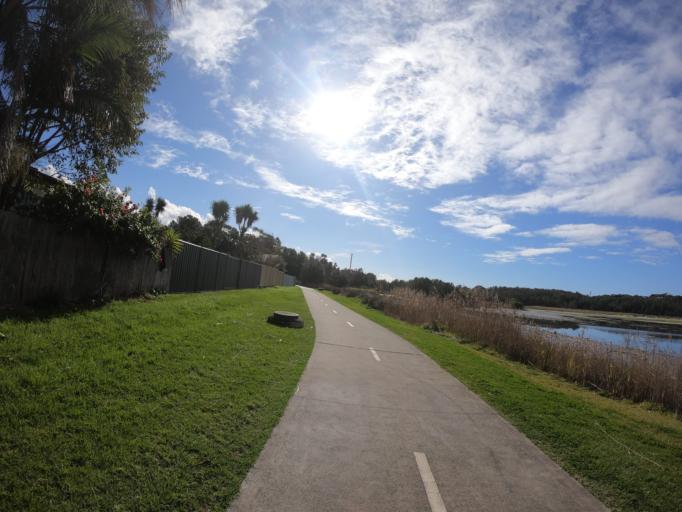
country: AU
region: New South Wales
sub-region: Wollongong
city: East Corrimal
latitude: -34.3731
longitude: 150.9197
